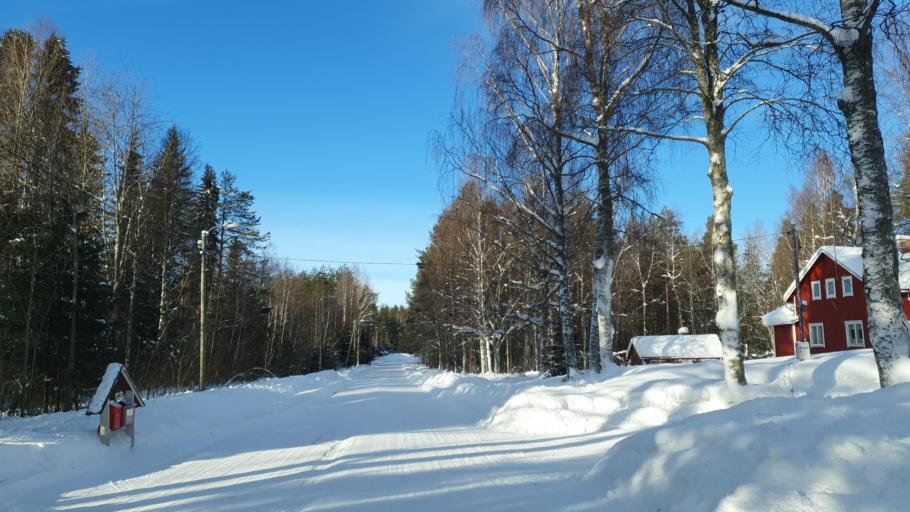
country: FI
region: Northern Ostrobothnia
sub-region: Oulu
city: Haukipudas
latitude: 65.1923
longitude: 25.4219
